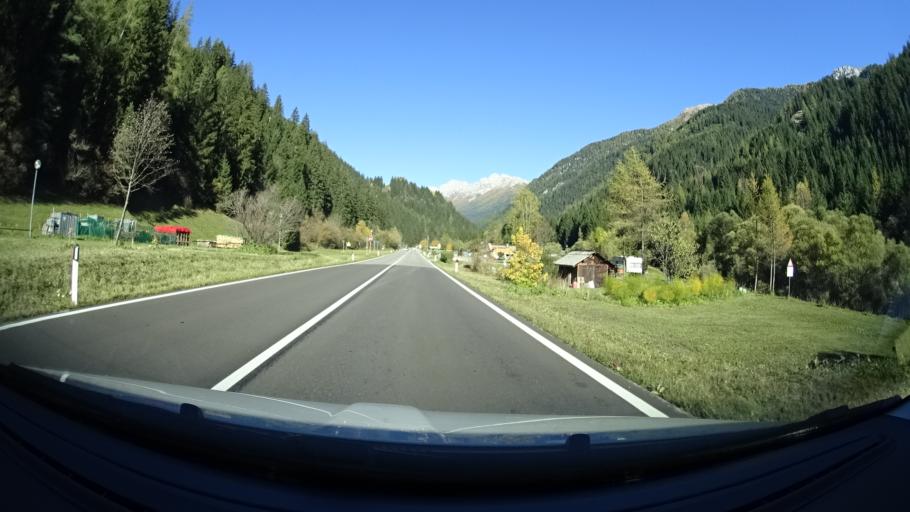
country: IT
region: Trentino-Alto Adige
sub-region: Provincia di Trento
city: Moena
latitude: 46.3512
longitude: 11.6301
